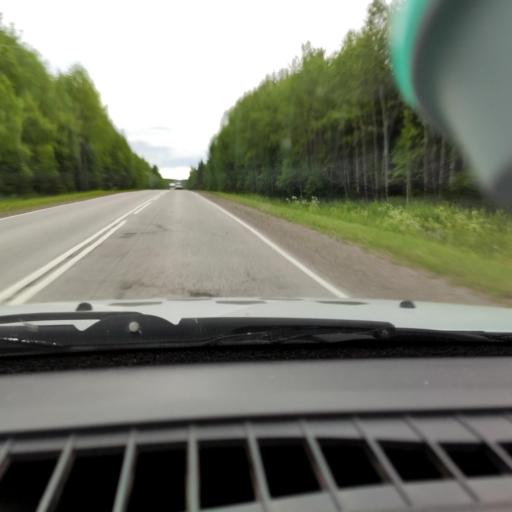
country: RU
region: Perm
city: Lys'va
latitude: 58.1249
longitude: 57.7200
